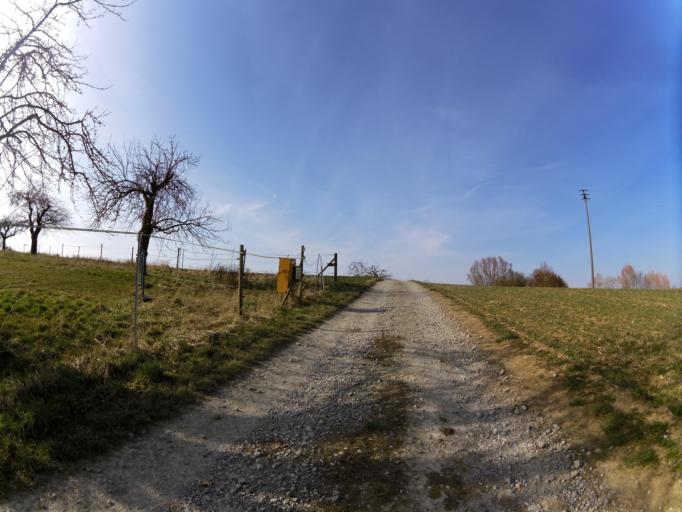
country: DE
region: Bavaria
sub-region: Regierungsbezirk Unterfranken
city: Prosselsheim
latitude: 49.8240
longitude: 10.1130
